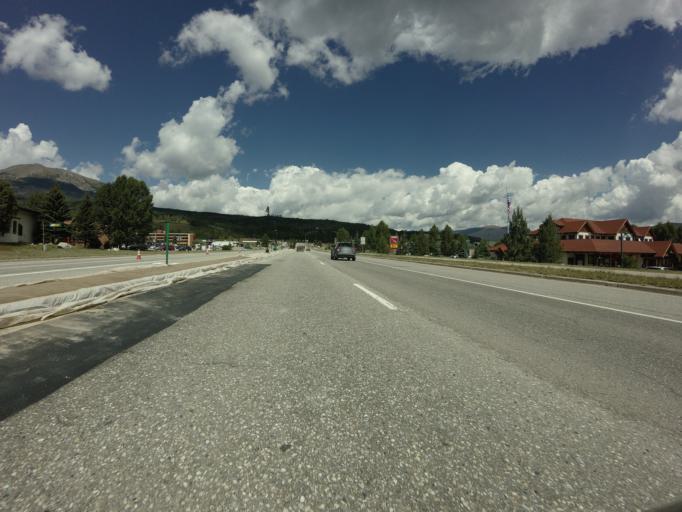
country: US
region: Colorado
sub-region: Summit County
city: Frisco
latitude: 39.5885
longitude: -106.0949
